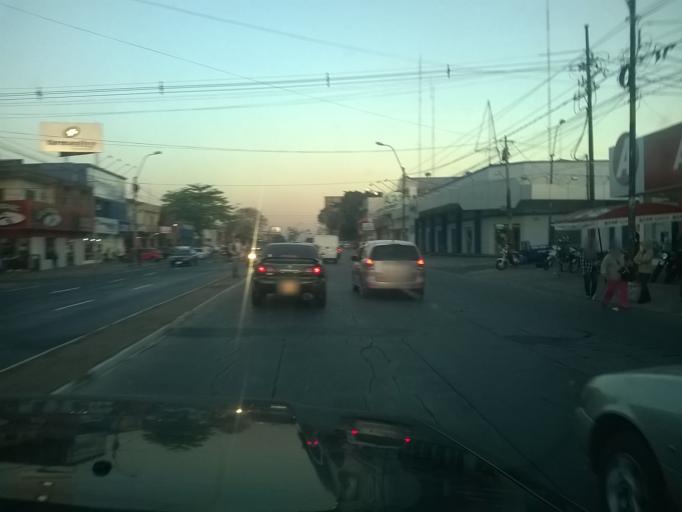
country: PY
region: Asuncion
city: Asuncion
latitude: -25.3055
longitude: -57.6060
